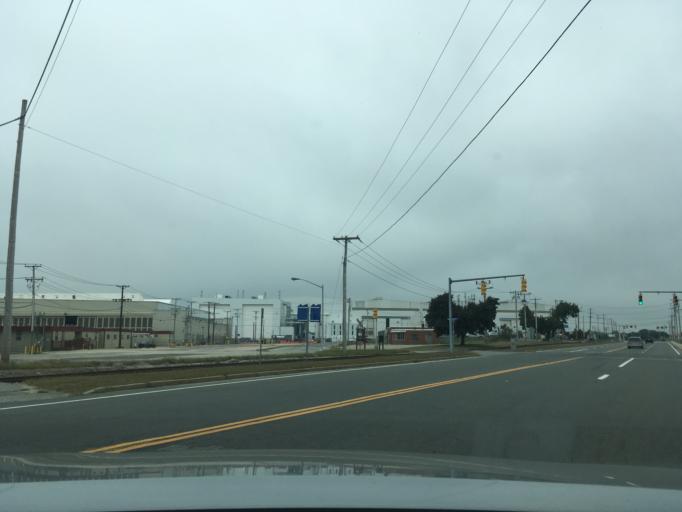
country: US
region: Rhode Island
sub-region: Washington County
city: North Kingstown
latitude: 41.5889
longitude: -71.4184
